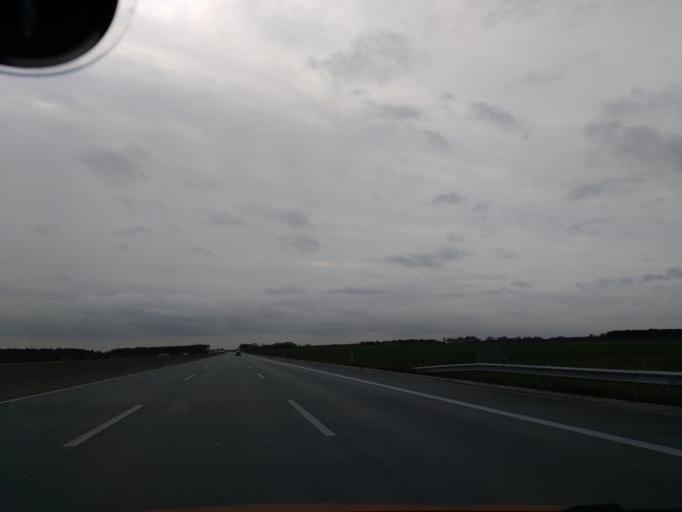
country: DE
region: Lower Saxony
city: Gross Meckelsen
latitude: 53.2731
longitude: 9.4589
